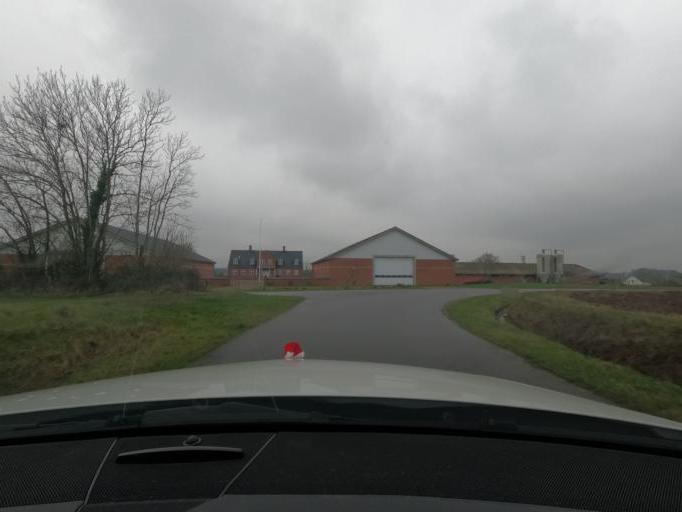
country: DK
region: South Denmark
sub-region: Haderslev Kommune
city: Starup
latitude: 55.1989
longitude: 9.6400
